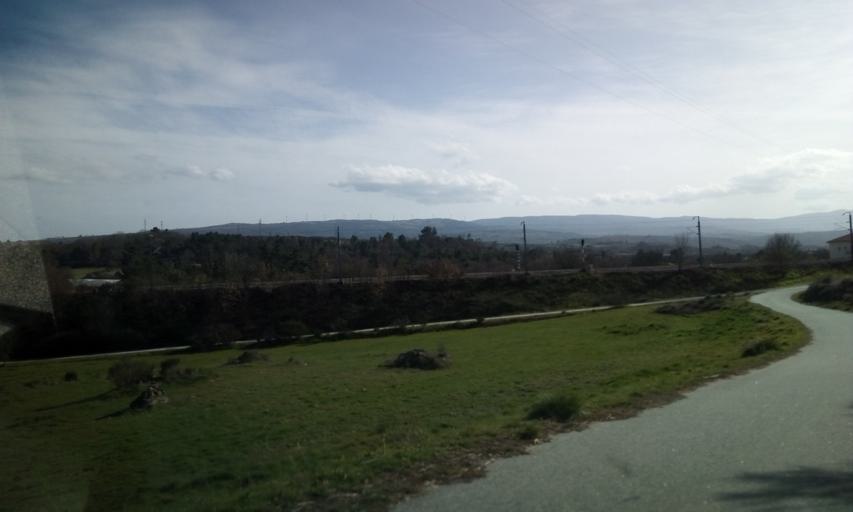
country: PT
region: Guarda
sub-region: Celorico da Beira
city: Celorico da Beira
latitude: 40.6441
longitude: -7.4285
